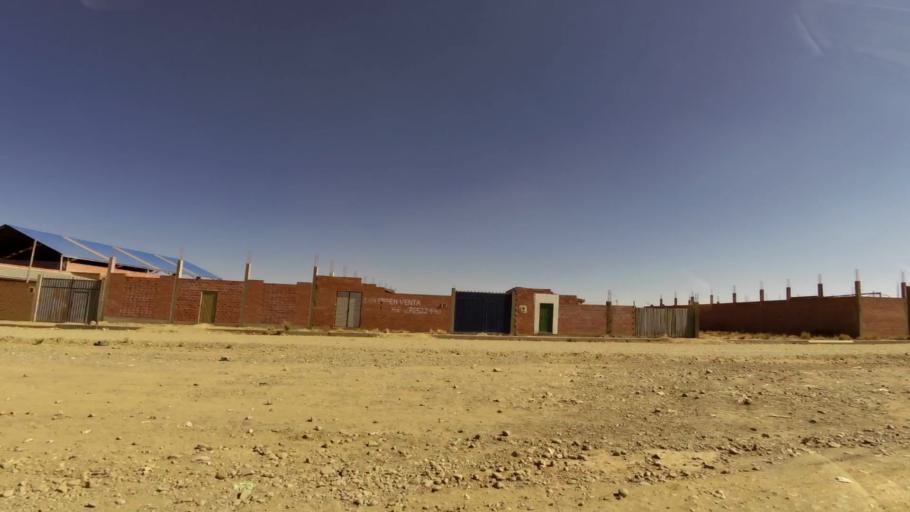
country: BO
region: La Paz
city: La Paz
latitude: -16.6000
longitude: -68.2013
